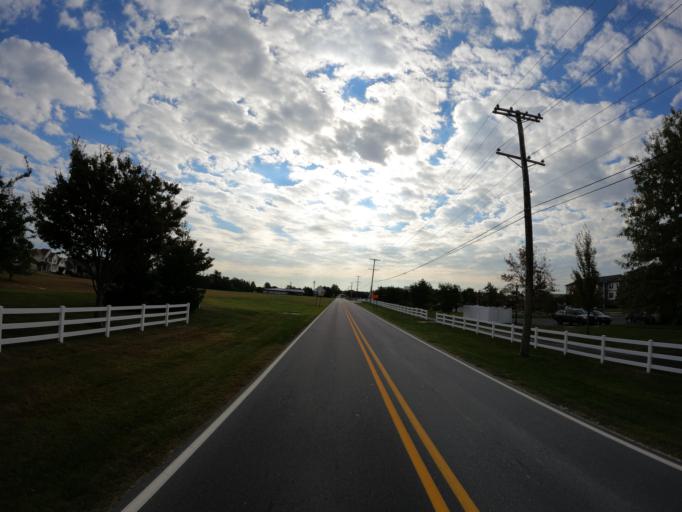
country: US
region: Delaware
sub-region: Sussex County
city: Lewes
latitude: 38.7539
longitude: -75.1685
